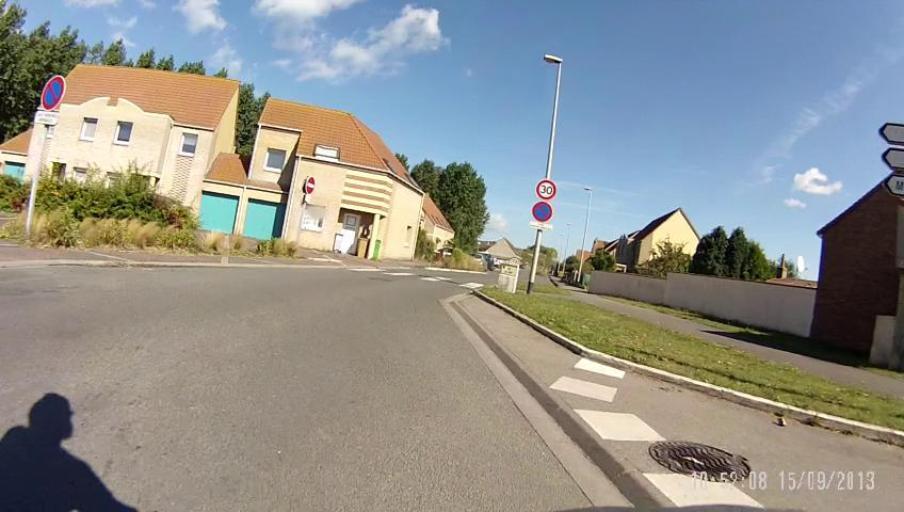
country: FR
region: Nord-Pas-de-Calais
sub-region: Departement du Nord
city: Leffrinckoucke
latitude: 51.0536
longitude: 2.4546
